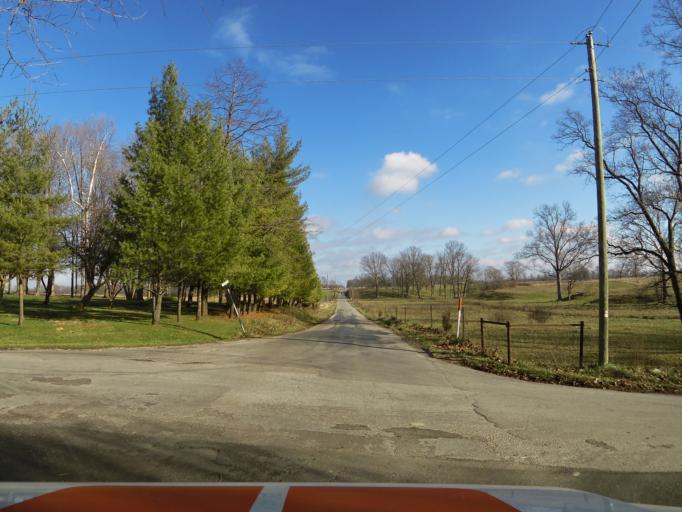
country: US
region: Indiana
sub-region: Jennings County
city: Country Squire Lakes
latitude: 38.9833
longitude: -85.7779
